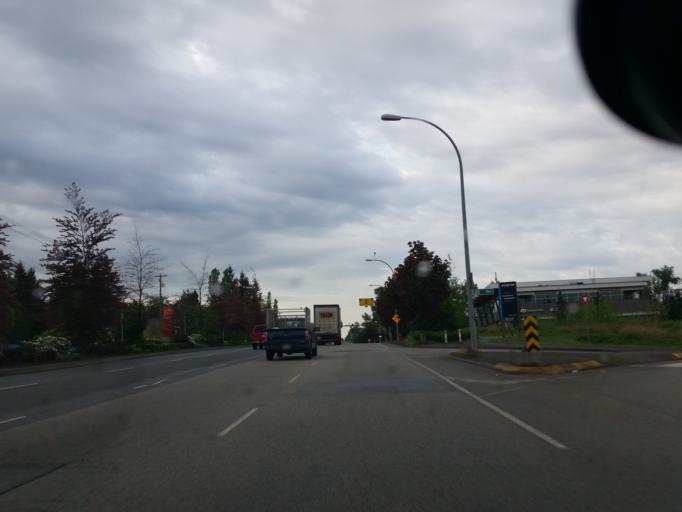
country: CA
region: British Columbia
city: Walnut Grove
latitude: 49.1576
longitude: -122.6682
